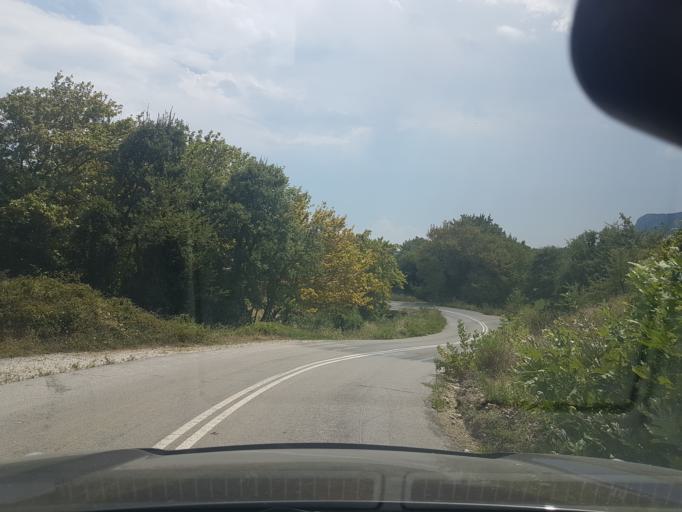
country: GR
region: Central Greece
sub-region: Nomos Evvoias
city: Kymi
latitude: 38.6495
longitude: 24.0338
